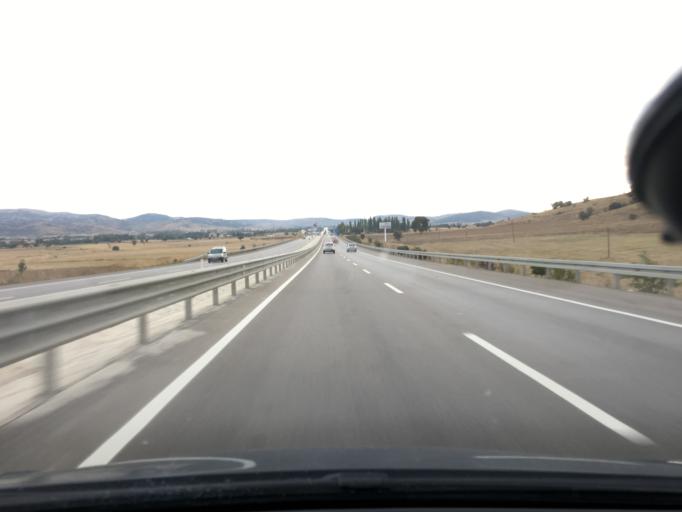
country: TR
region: Afyonkarahisar
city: Sincanli
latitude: 38.6431
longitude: 30.3087
